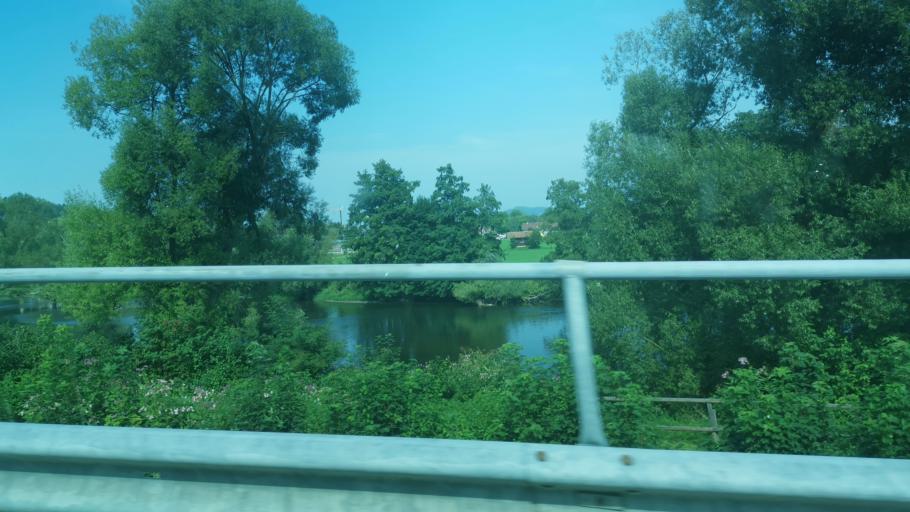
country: DE
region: Bavaria
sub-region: Upper Palatinate
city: Chamerau
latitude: 49.1981
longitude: 12.7507
